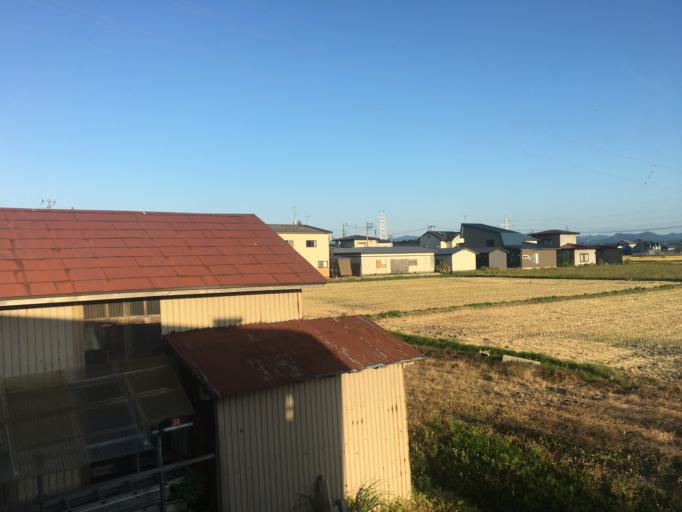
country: JP
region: Akita
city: Takanosu
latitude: 40.2238
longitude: 140.3574
